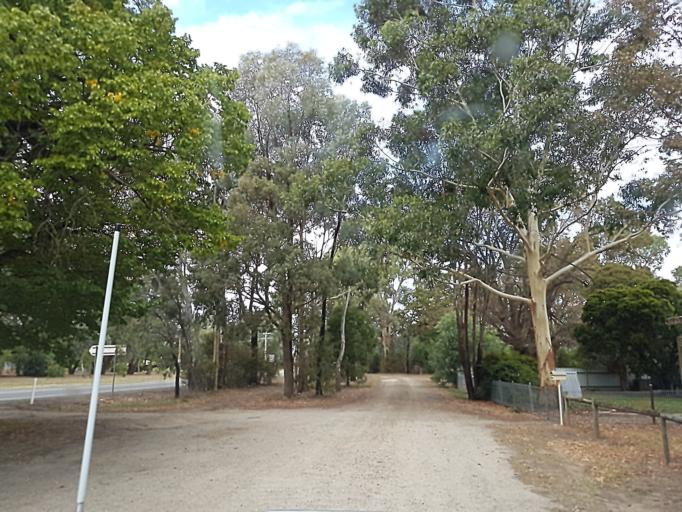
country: AU
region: Victoria
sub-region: Wangaratta
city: Wangaratta
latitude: -36.3913
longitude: 146.4459
